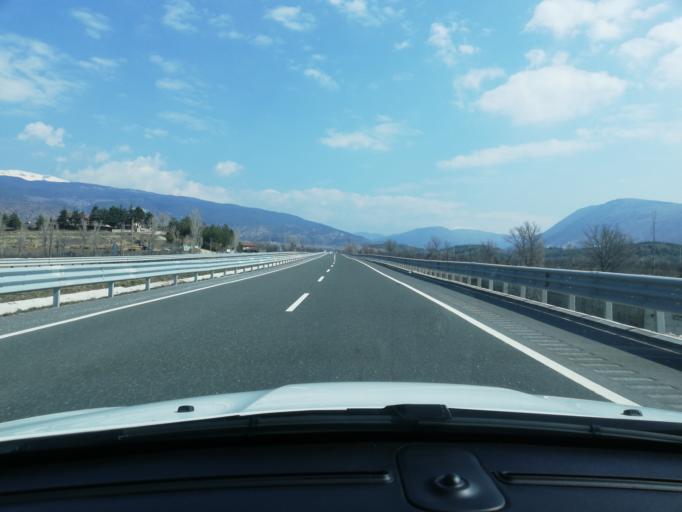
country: TR
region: Cankiri
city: Ilgaz
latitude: 40.9345
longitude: 33.6546
